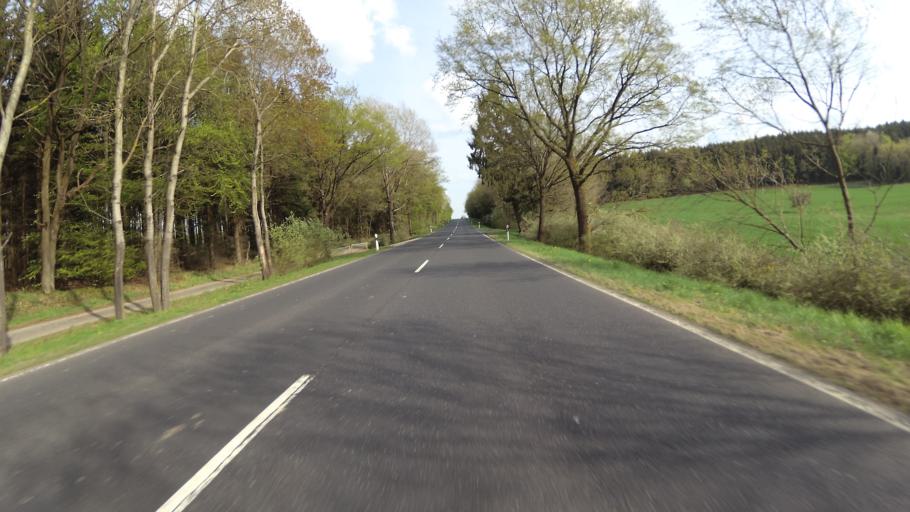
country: DE
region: Rheinland-Pfalz
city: Berenbach
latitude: 50.2345
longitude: 6.9376
